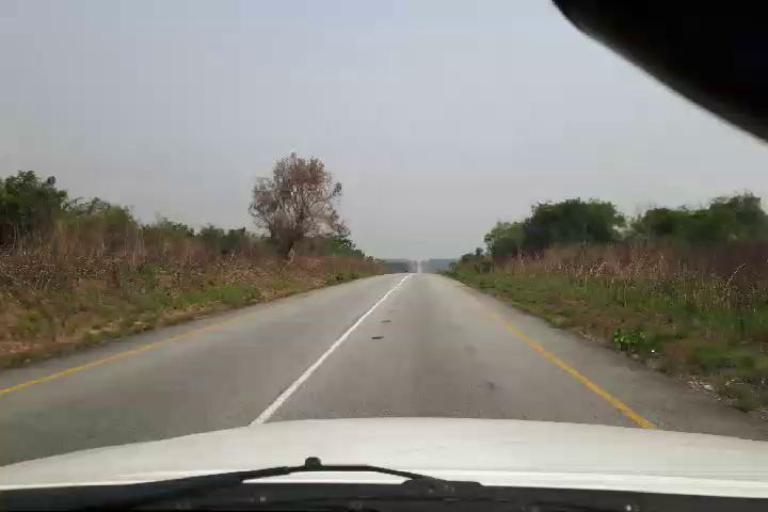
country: SL
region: Southern Province
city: Largo
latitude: 8.2409
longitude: -12.0853
